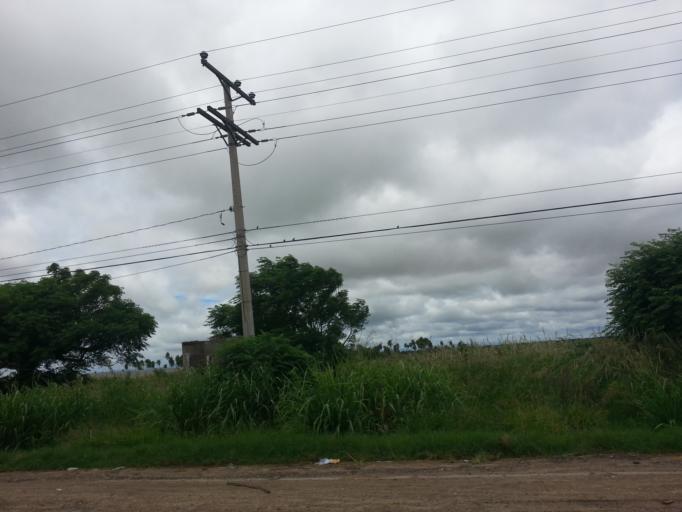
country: BO
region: Santa Cruz
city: La Belgica
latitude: -17.6191
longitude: -63.1592
